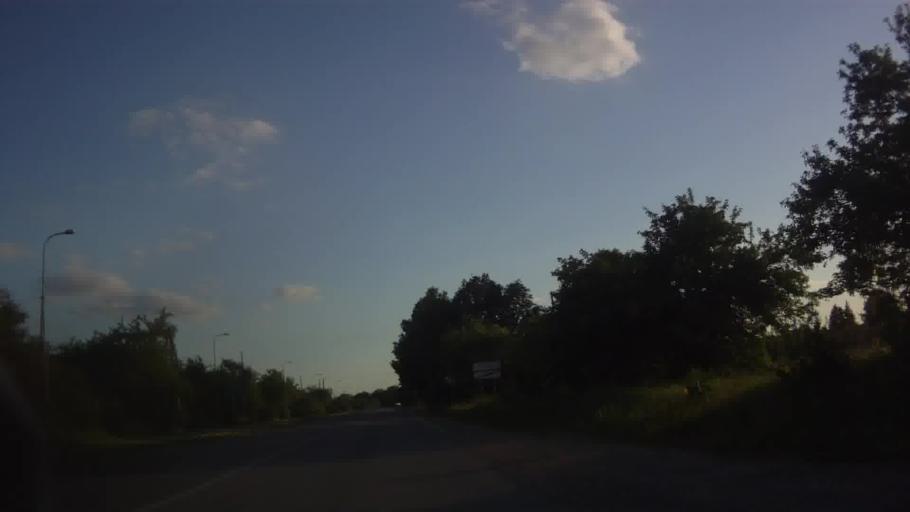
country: LV
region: Jekabpils Rajons
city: Jekabpils
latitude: 56.5128
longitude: 25.9301
